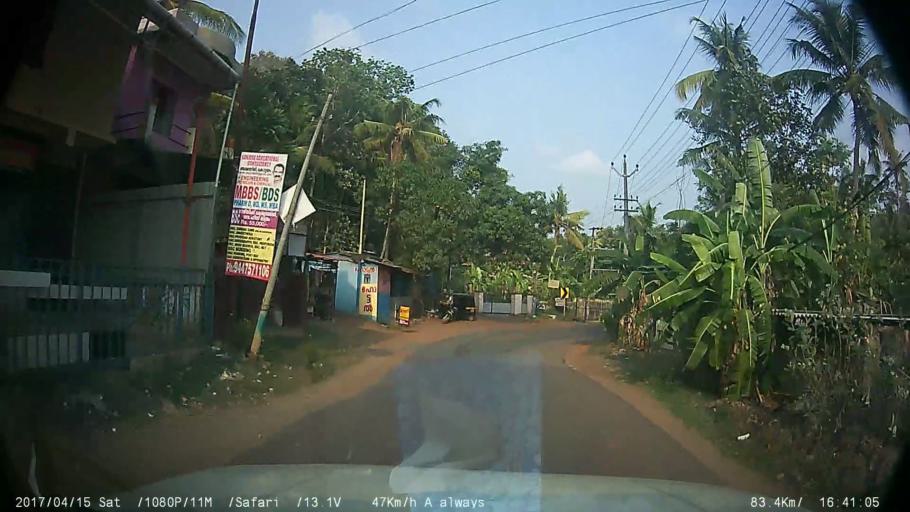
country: IN
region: Kerala
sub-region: Kottayam
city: Kottayam
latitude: 9.6462
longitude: 76.5265
